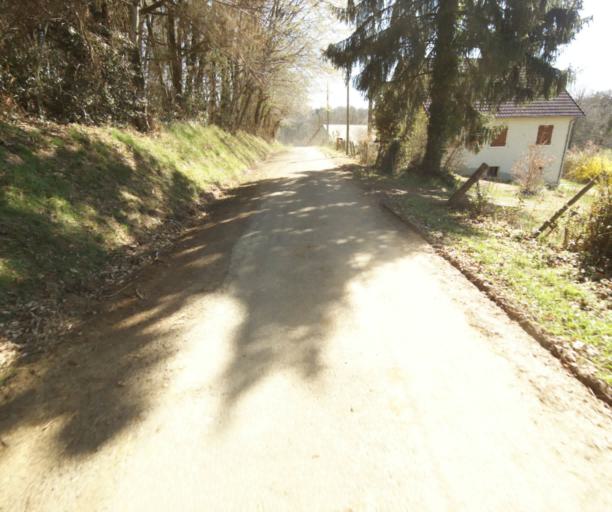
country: FR
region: Limousin
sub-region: Departement de la Correze
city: Saint-Clement
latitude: 45.3939
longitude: 1.6603
